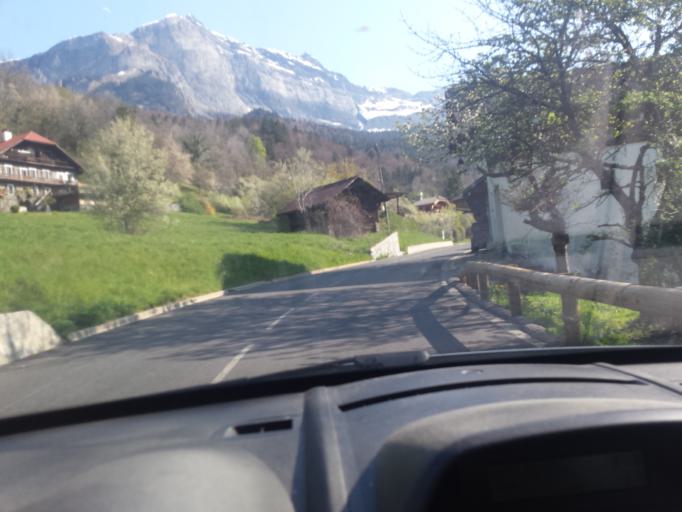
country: FR
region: Rhone-Alpes
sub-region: Departement de la Haute-Savoie
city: Passy
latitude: 45.9307
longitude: 6.7135
